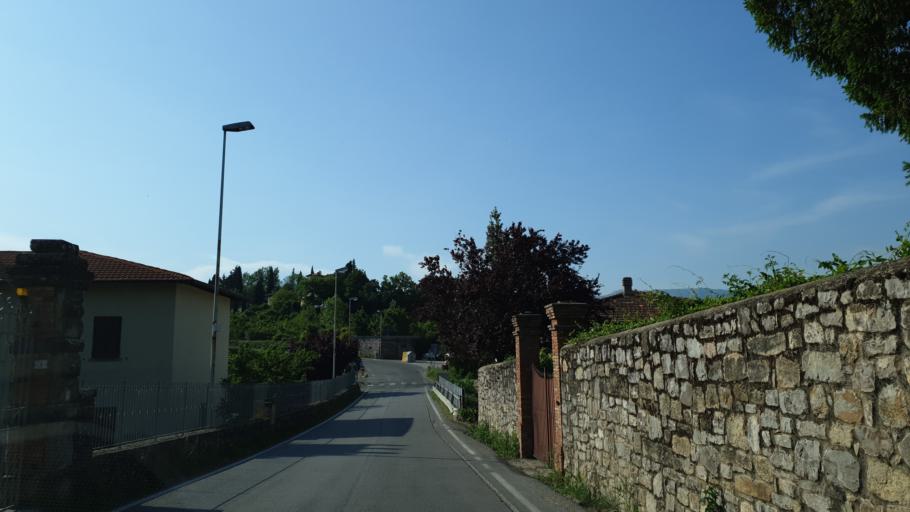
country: IT
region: Tuscany
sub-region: Province of Arezzo
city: Strada
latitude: 43.7515
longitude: 11.7234
